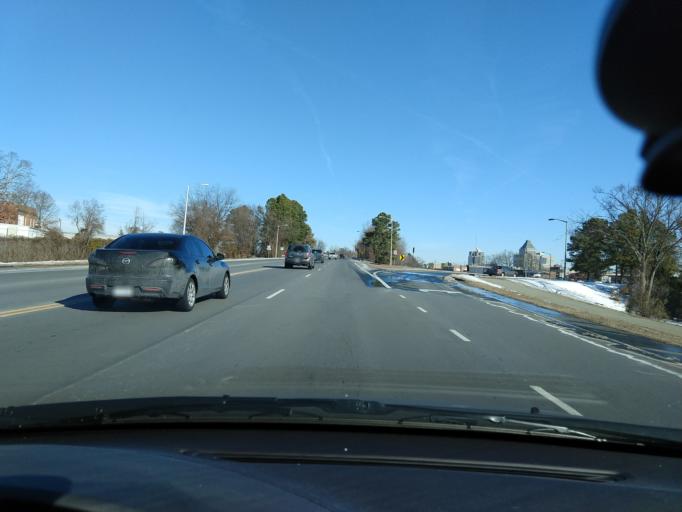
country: US
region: North Carolina
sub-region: Guilford County
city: Greensboro
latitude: 36.0622
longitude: -79.8000
